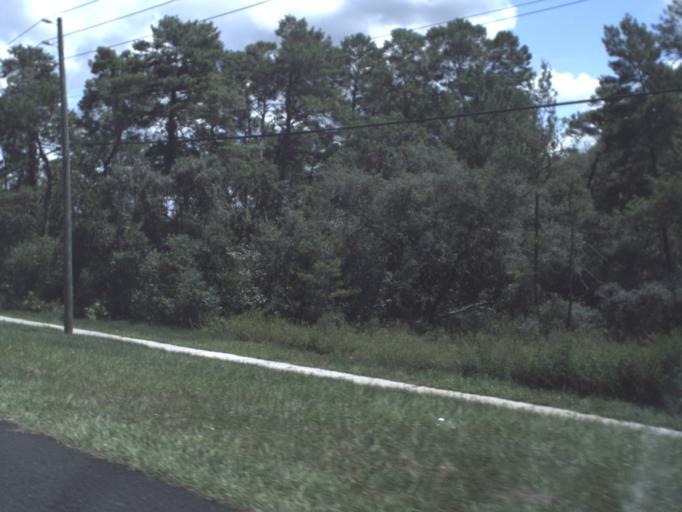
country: US
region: Florida
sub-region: Hernando County
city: North Weeki Wachee
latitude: 28.5237
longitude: -82.5697
